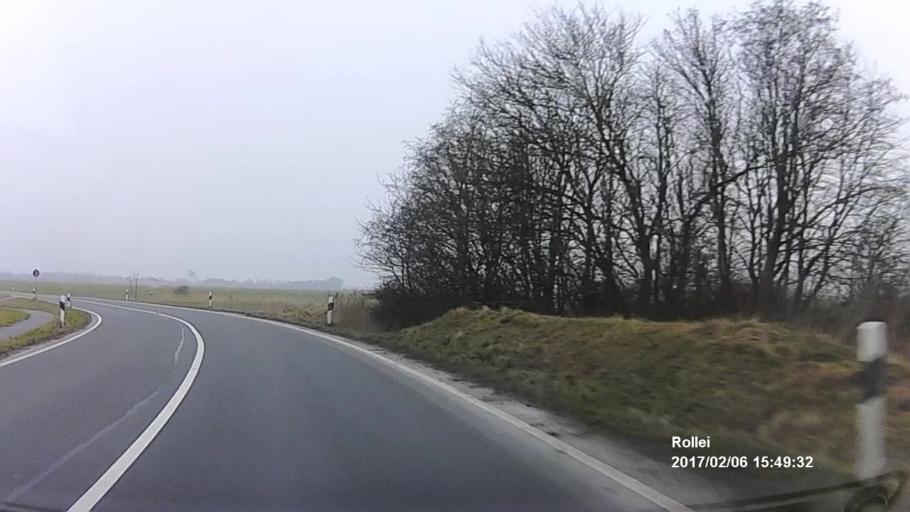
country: DE
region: Lower Saxony
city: Wirdum
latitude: 53.4895
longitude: 7.1260
